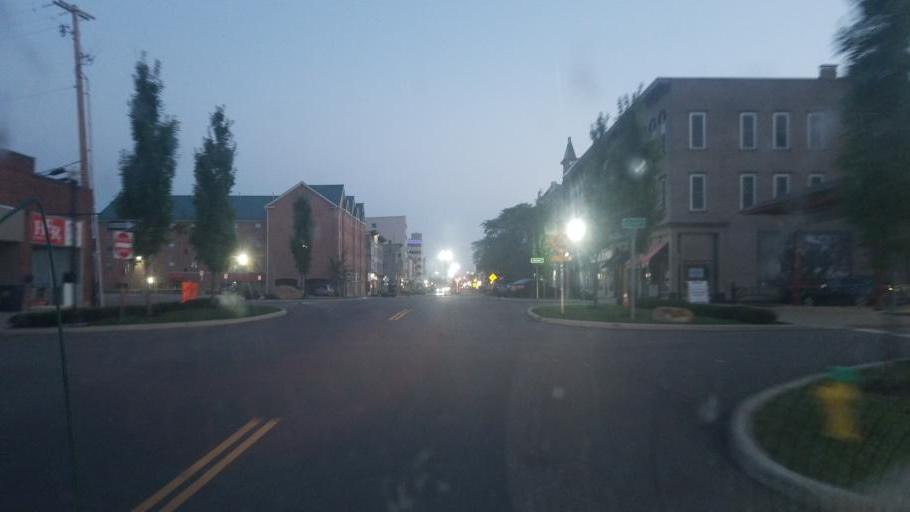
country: US
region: Ohio
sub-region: Licking County
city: Newark
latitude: 40.0561
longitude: -82.4018
